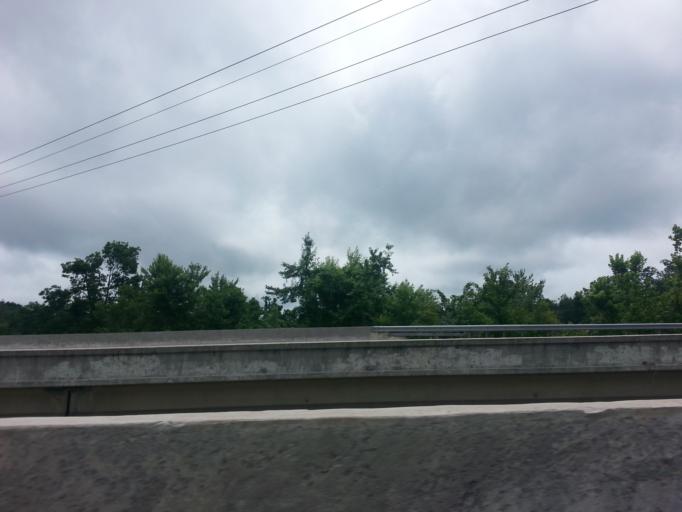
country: US
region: Tennessee
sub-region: Putnam County
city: Monterey
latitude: 36.1001
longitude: -85.2362
